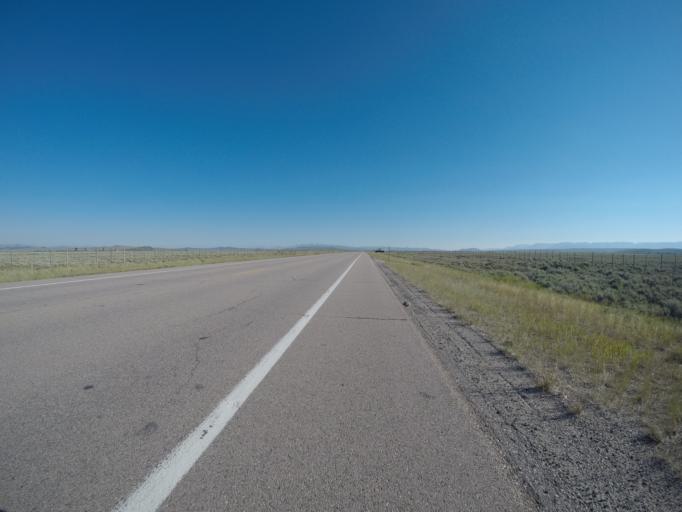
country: US
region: Wyoming
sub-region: Sublette County
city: Pinedale
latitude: 42.9543
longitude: -110.0867
